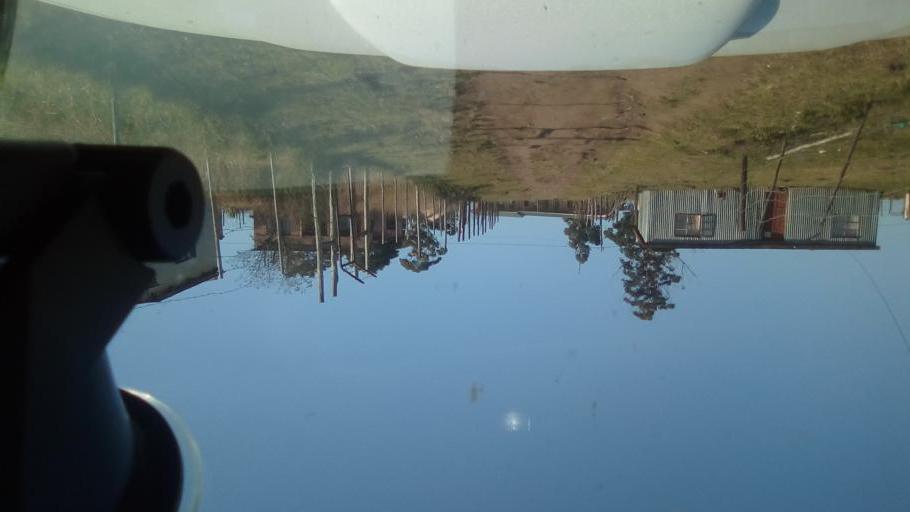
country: ZA
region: Eastern Cape
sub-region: Buffalo City Metropolitan Municipality
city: Bhisho
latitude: -32.7978
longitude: 27.3479
